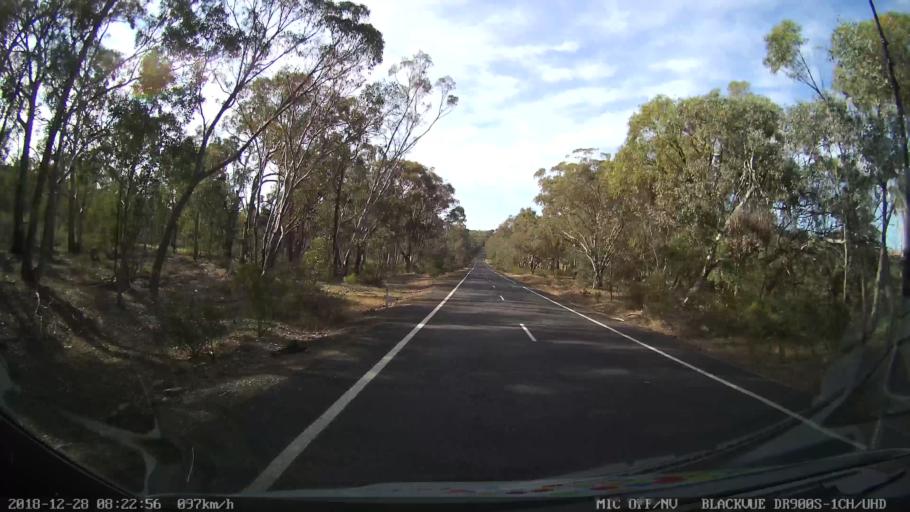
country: AU
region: New South Wales
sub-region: Blayney
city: Blayney
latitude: -33.8997
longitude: 149.3484
